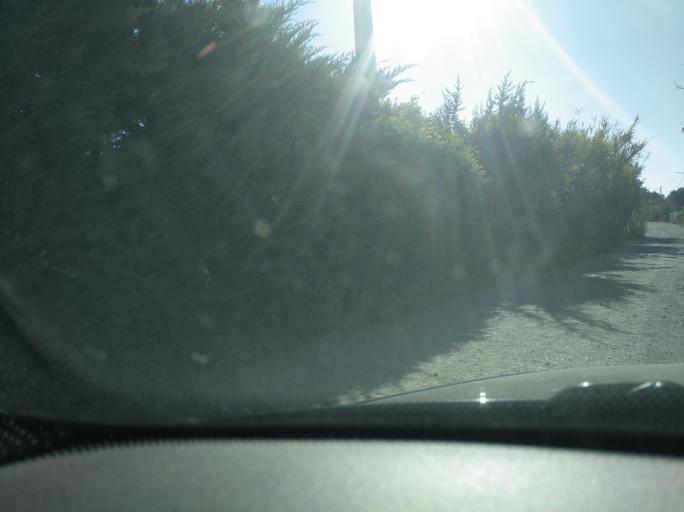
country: PT
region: Faro
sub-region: Vila Real de Santo Antonio
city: Monte Gordo
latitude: 37.1726
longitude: -7.5101
